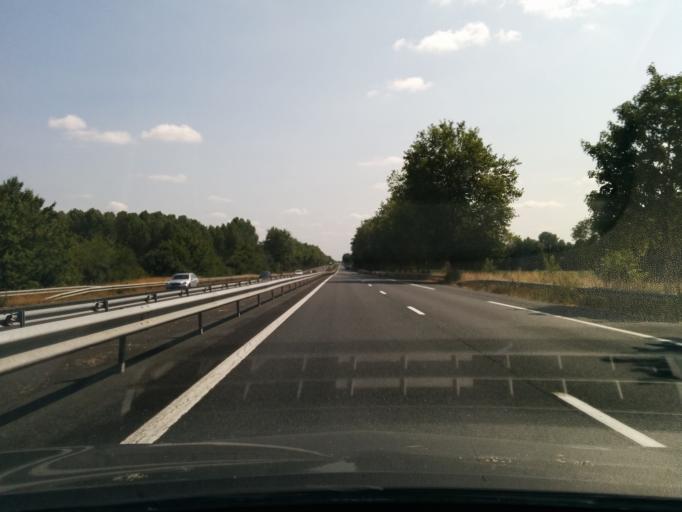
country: FR
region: Centre
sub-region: Departement de l'Indre
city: Montierchaume
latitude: 46.9263
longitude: 1.7444
